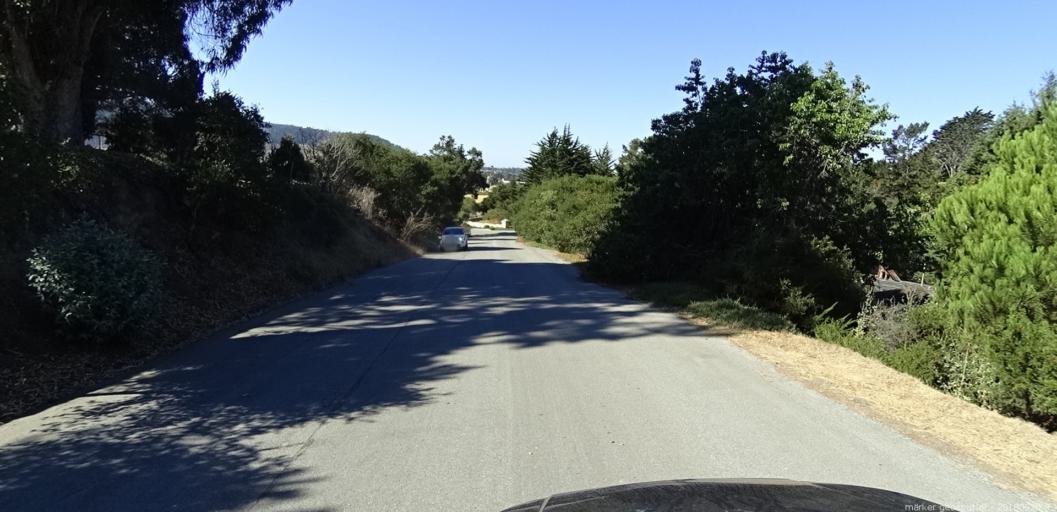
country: US
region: California
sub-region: Monterey County
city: Carmel-by-the-Sea
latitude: 36.5453
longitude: -121.8988
